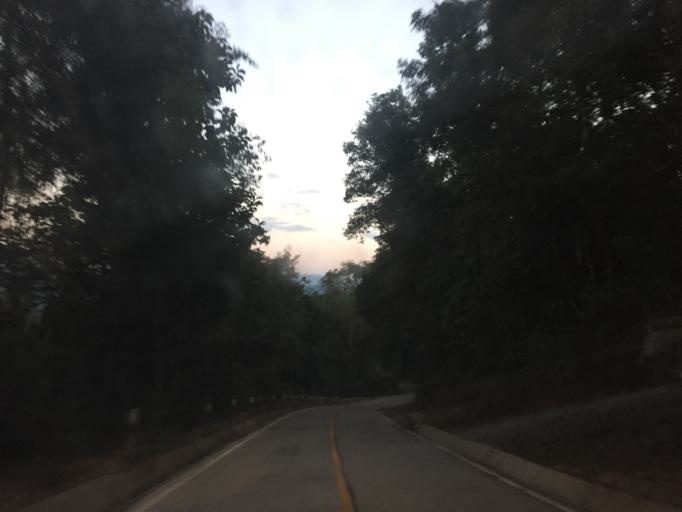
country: TH
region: Chiang Mai
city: Samoeng
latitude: 18.9895
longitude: 98.7192
